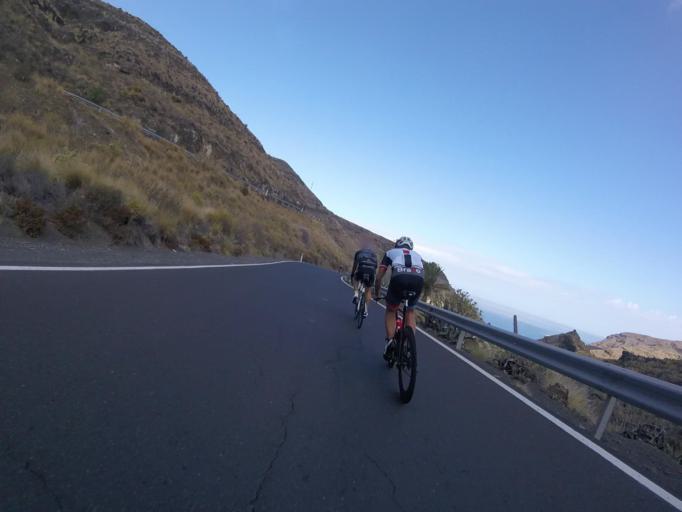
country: ES
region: Canary Islands
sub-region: Provincia de Las Palmas
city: Agaete
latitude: 28.0769
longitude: -15.7044
